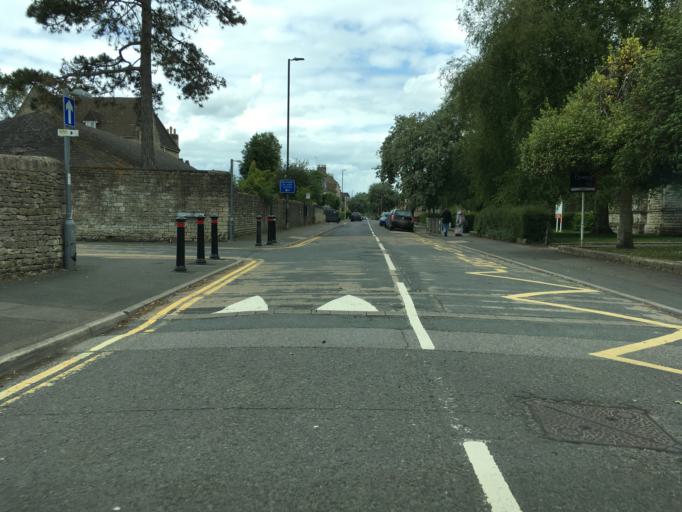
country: GB
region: England
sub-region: Gloucestershire
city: Cirencester
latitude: 51.7115
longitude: -1.9602
